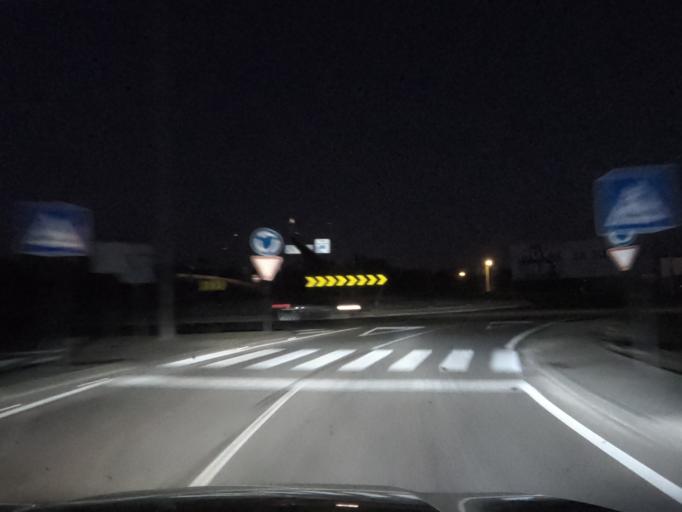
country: PT
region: Faro
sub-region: Loule
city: Loule
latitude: 37.1322
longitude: -8.0381
